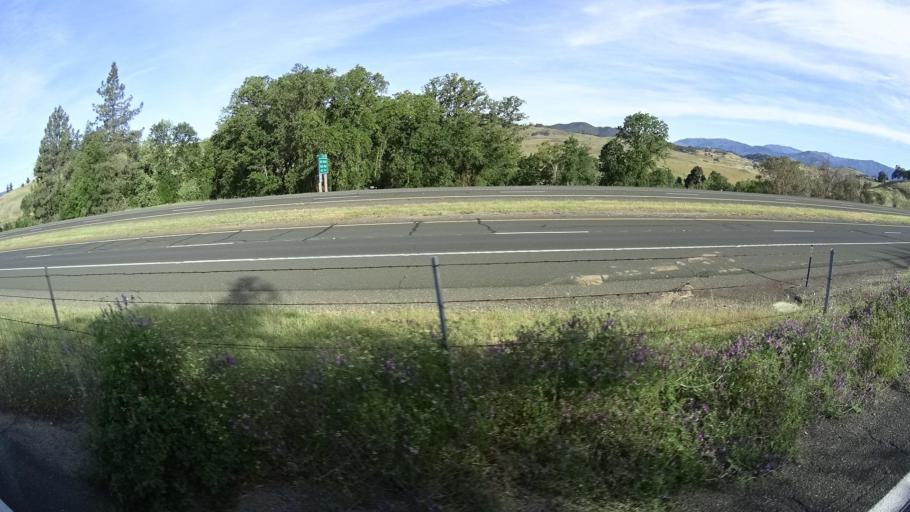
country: US
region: California
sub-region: Lake County
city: North Lakeport
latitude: 39.0910
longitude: -122.9163
